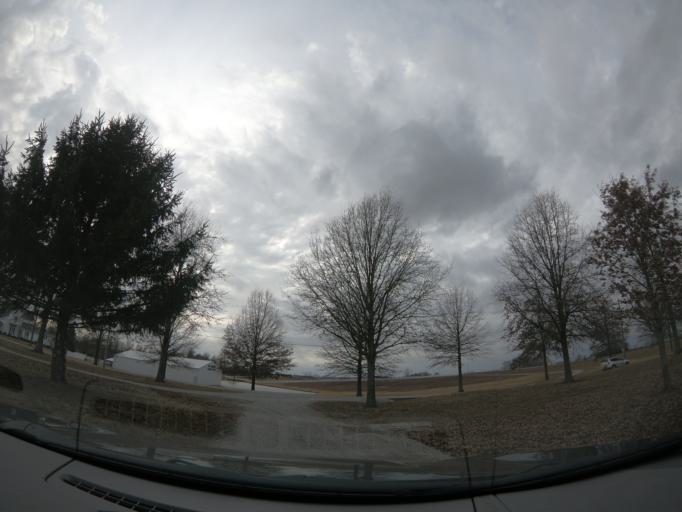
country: US
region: Indiana
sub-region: Floyd County
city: Galena
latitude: 38.4161
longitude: -85.9153
